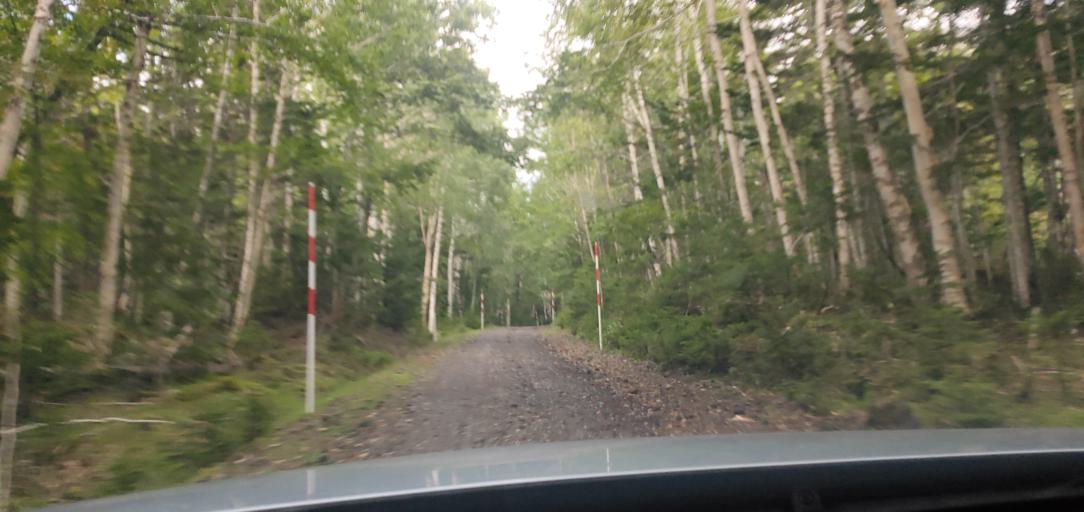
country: JP
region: Hokkaido
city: Kitami
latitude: 43.3736
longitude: 143.9656
